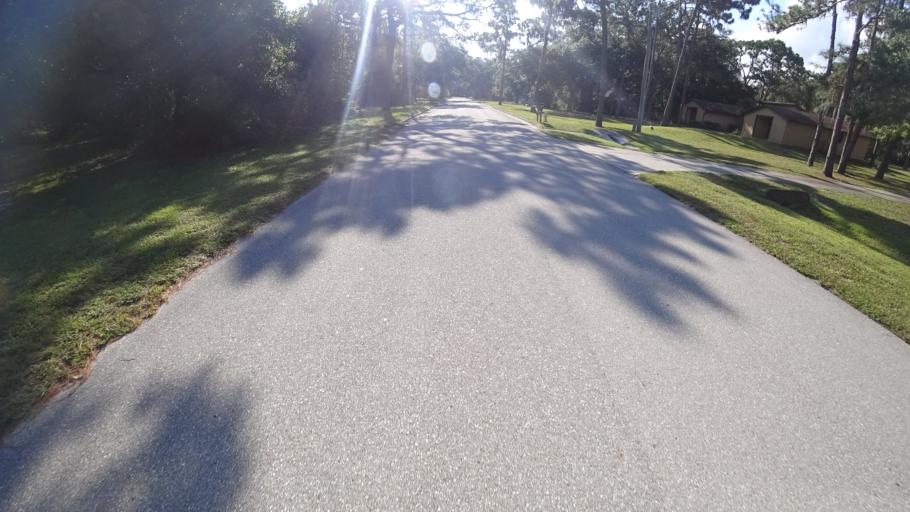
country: US
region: Florida
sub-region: Sarasota County
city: The Meadows
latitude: 27.4242
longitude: -82.4499
